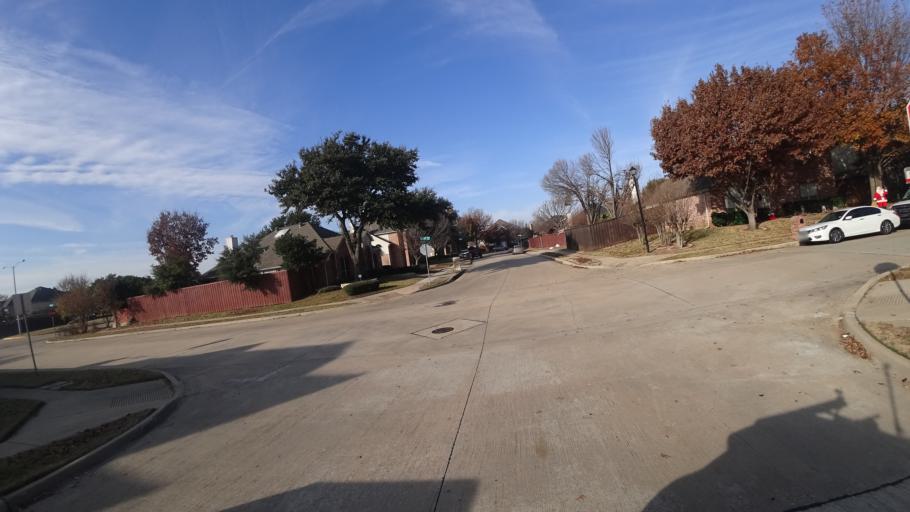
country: US
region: Texas
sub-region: Denton County
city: Lewisville
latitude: 33.0573
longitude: -97.0202
